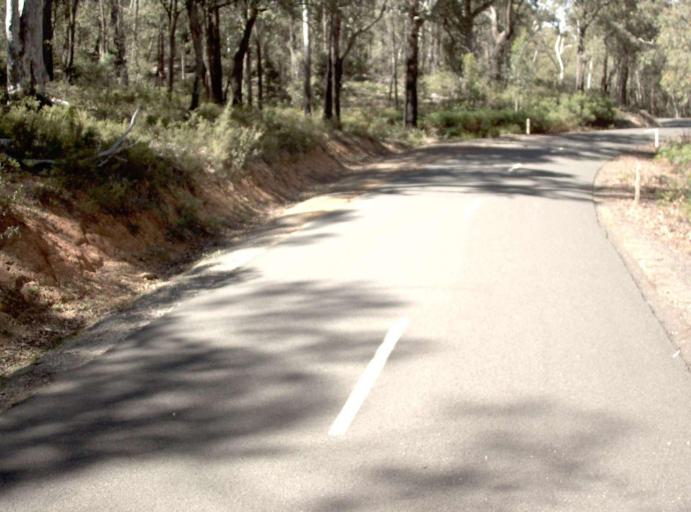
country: AU
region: New South Wales
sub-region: Bombala
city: Bombala
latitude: -37.1023
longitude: 148.7600
